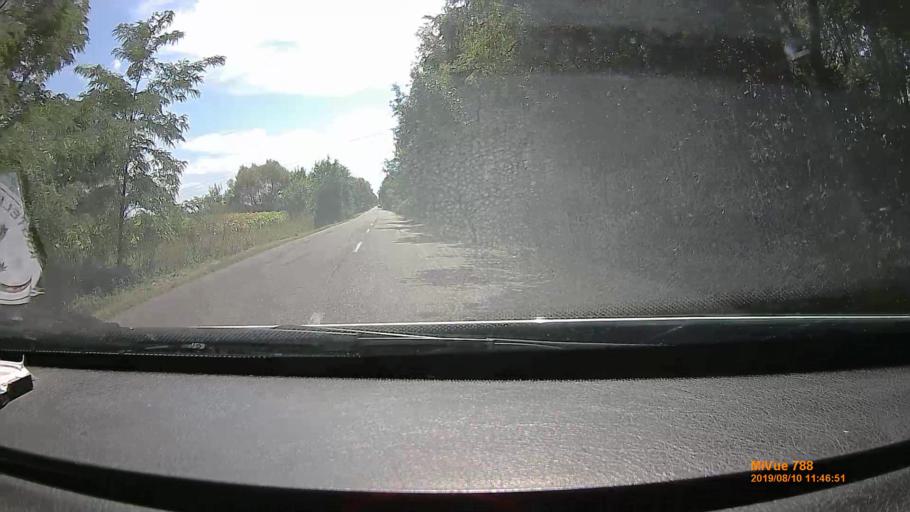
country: HU
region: Borsod-Abauj-Zemplen
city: Szentistvan
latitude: 47.7088
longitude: 20.6318
